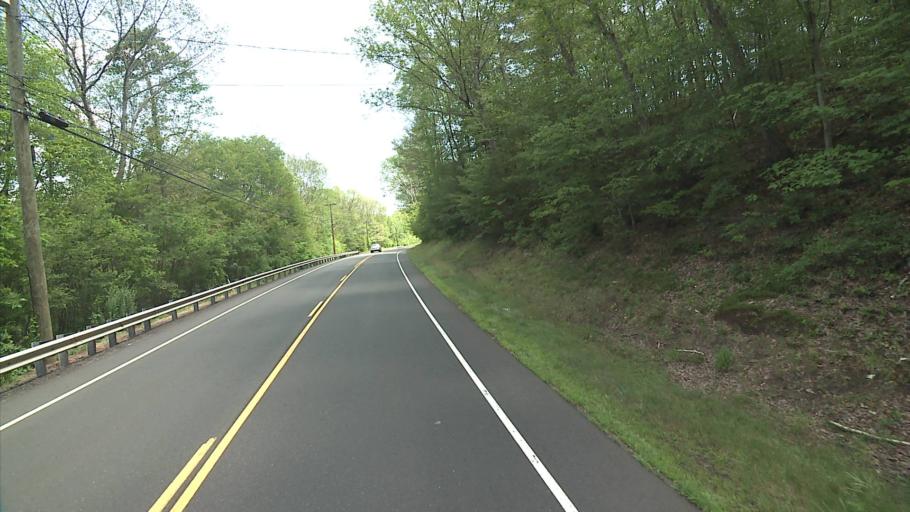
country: US
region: Connecticut
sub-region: Middlesex County
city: Higganum
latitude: 41.4958
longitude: -72.5345
